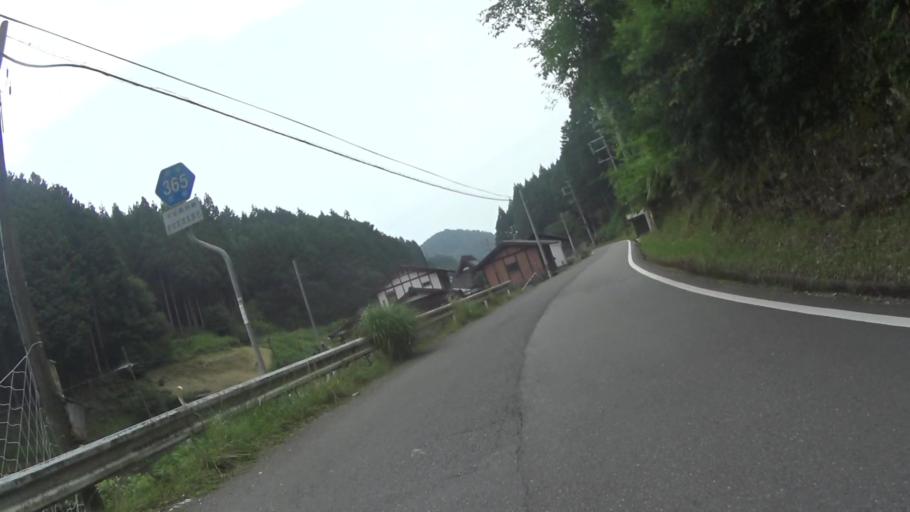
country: JP
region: Kyoto
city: Kameoka
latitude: 35.1554
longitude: 135.5959
